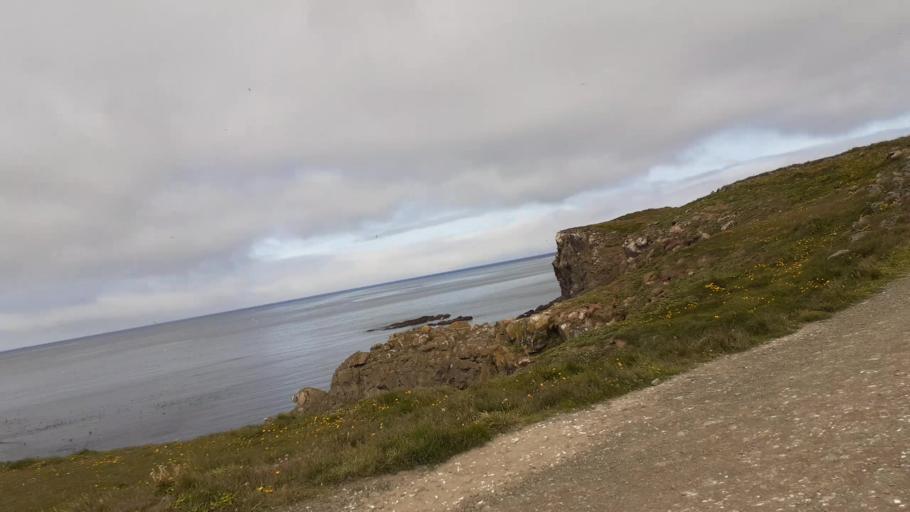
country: IS
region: Northeast
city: Dalvik
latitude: 66.5500
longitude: -18.0259
